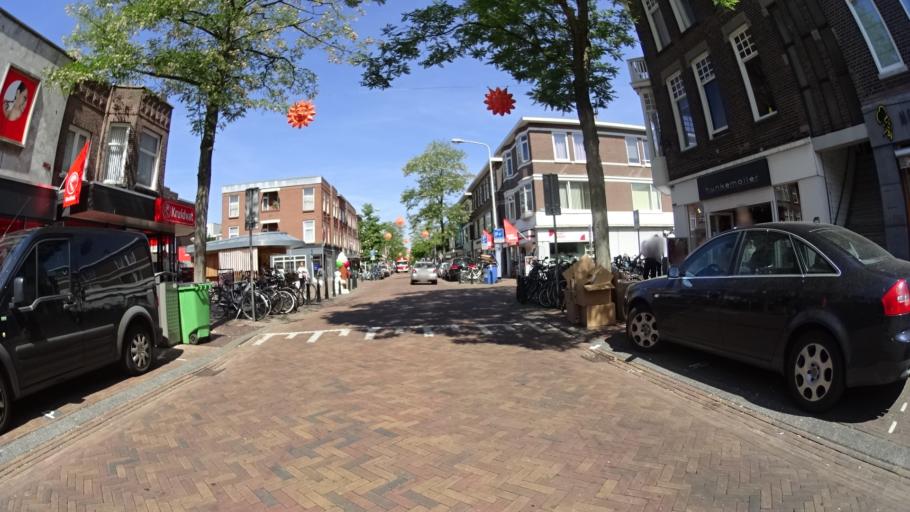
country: NL
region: South Holland
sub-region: Gemeente Den Haag
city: Scheveningen
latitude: 52.0775
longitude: 4.2706
